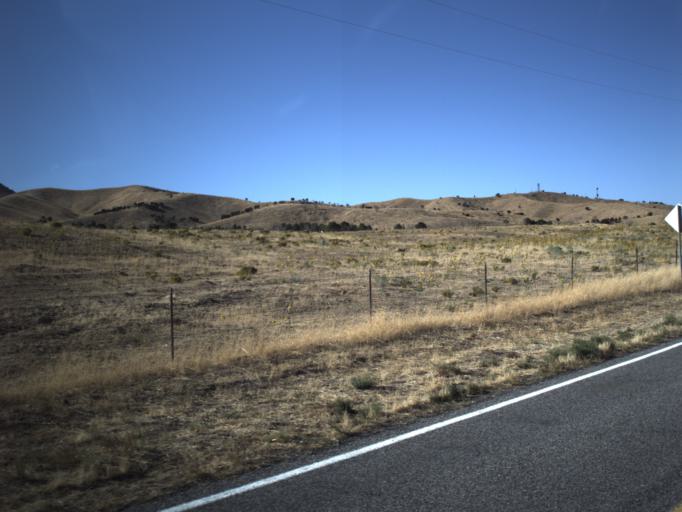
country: US
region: Utah
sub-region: Millard County
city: Delta
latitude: 39.3662
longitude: -112.3407
